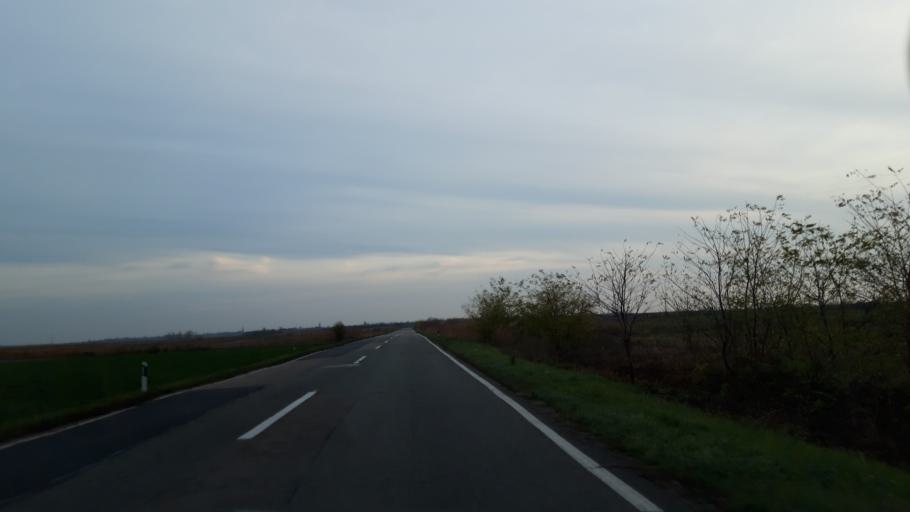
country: RS
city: Ostojicevo
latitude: 45.9132
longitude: 20.1513
